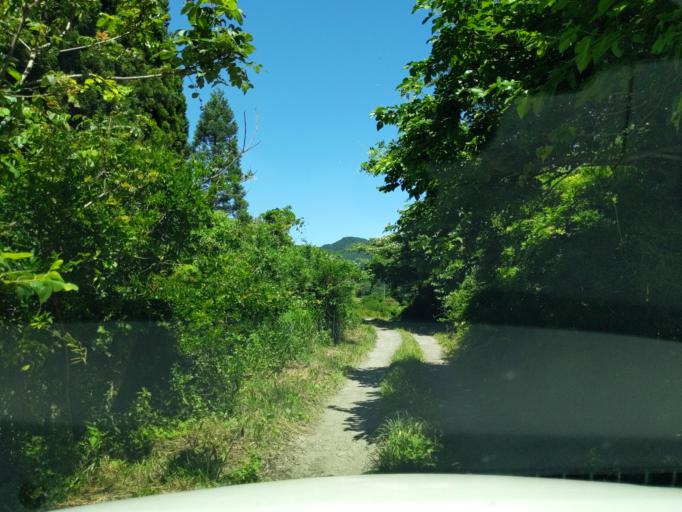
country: JP
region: Fukushima
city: Koriyama
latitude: 37.3883
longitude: 140.2482
